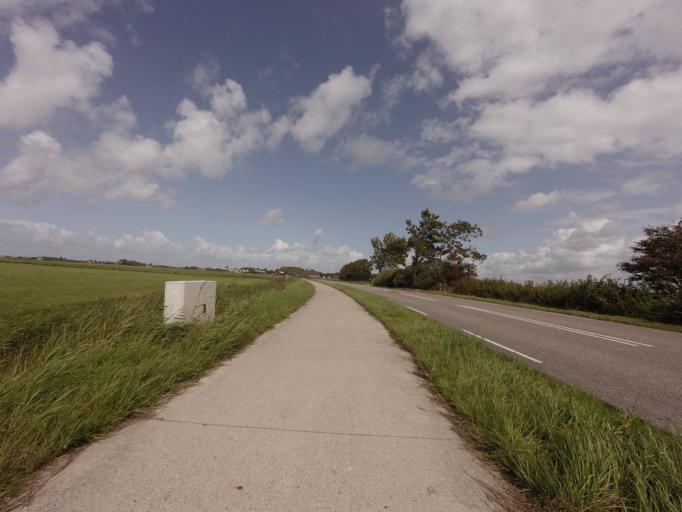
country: NL
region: Friesland
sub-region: Gemeente Harlingen
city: Harlingen
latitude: 53.1427
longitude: 5.4772
